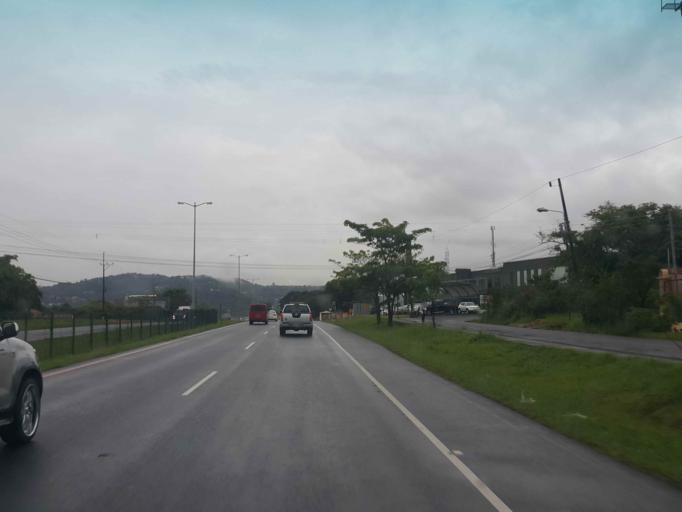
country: CR
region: San Jose
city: Santa Ana
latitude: 9.9388
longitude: -84.2048
